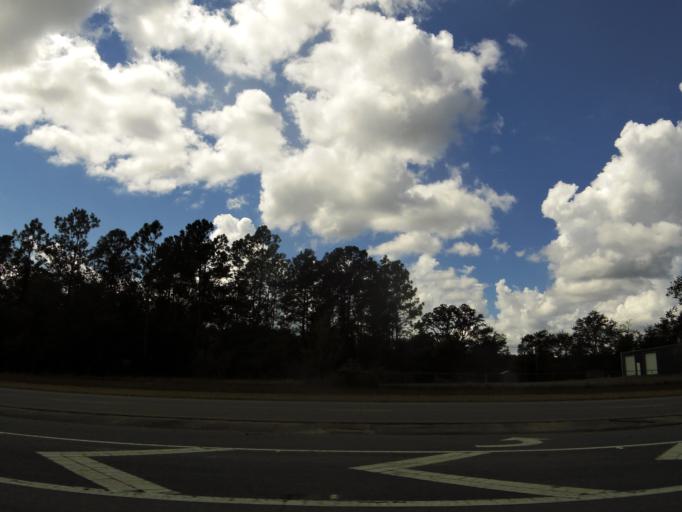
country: US
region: Georgia
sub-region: Charlton County
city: Folkston
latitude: 30.8088
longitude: -81.9967
